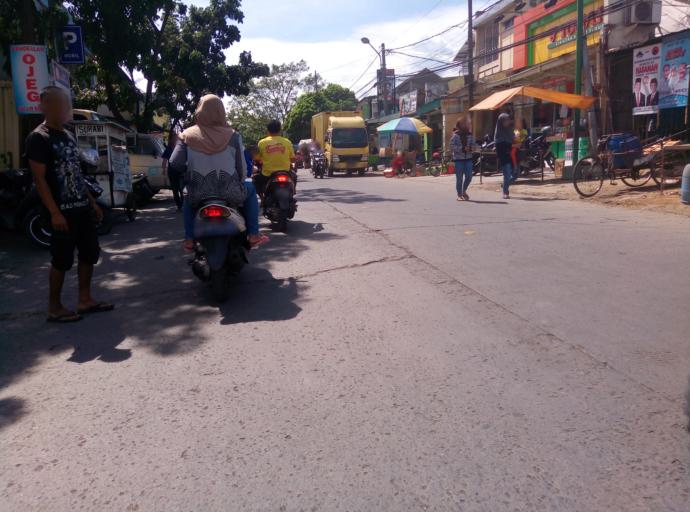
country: ID
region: West Java
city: Bandung
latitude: -6.9047
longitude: 107.6439
